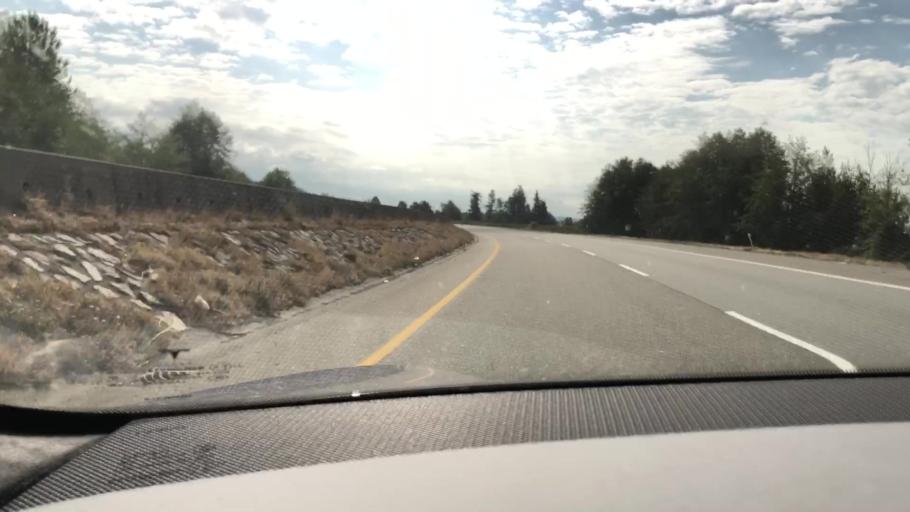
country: CA
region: British Columbia
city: Delta
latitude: 49.1170
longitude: -122.9249
